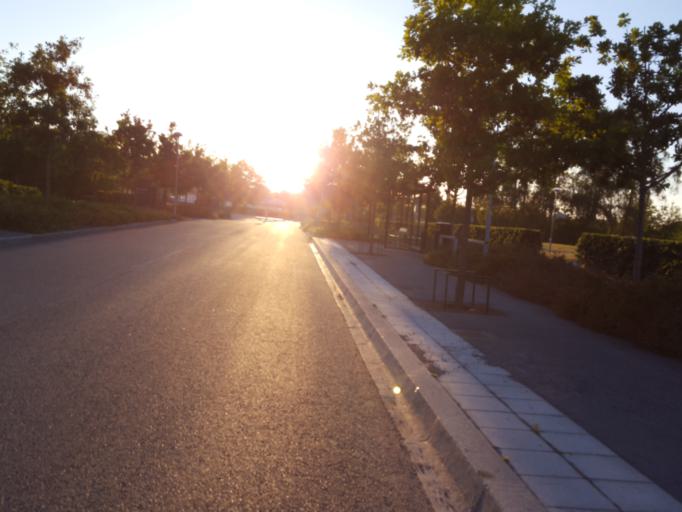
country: SE
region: Uppsala
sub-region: Uppsala Kommun
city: Saevja
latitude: 59.8184
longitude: 17.6590
